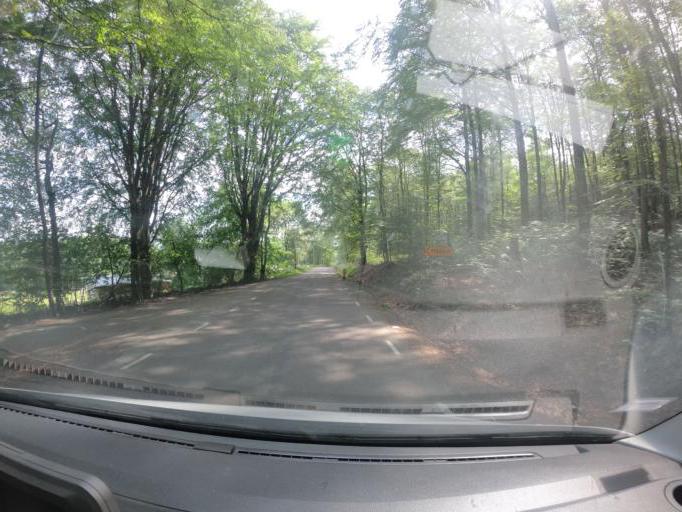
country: SE
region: Skane
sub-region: Bastads Kommun
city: Bastad
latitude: 56.4161
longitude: 12.9217
